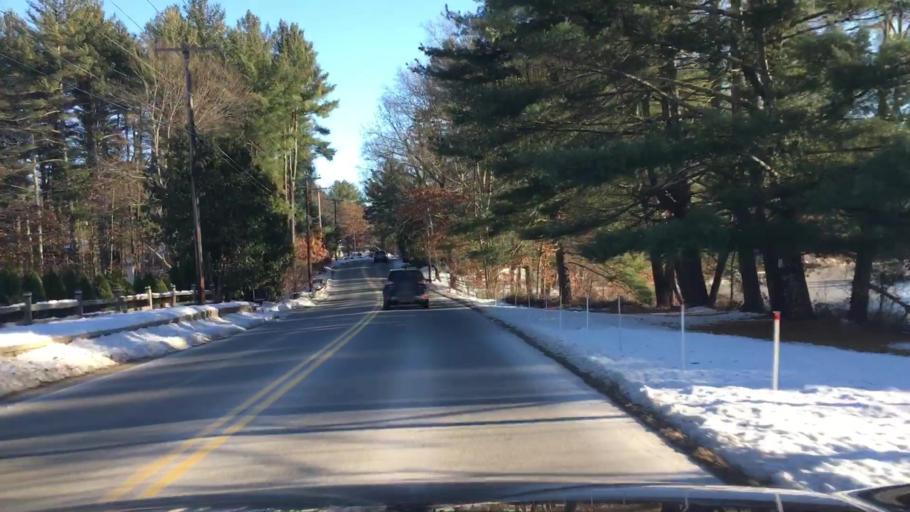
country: US
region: New Hampshire
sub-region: Hillsborough County
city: Hollis
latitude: 42.8077
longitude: -71.5579
